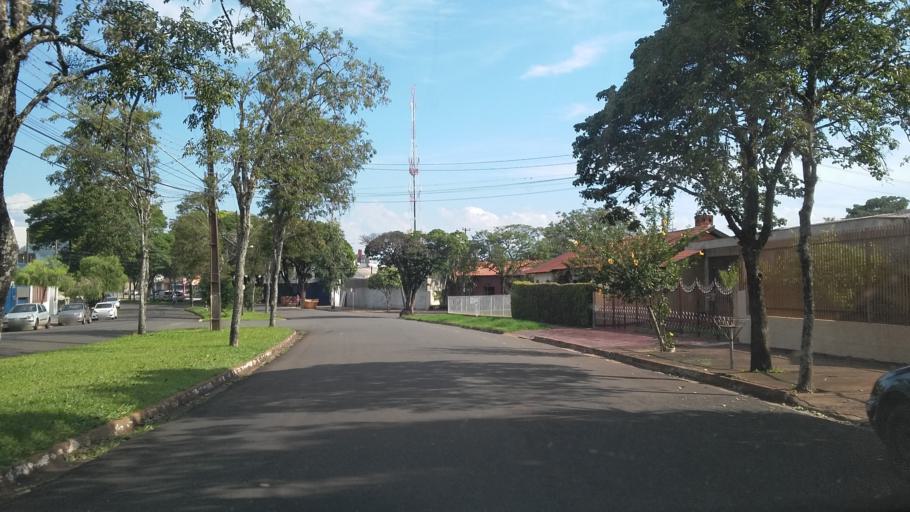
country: BR
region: Parana
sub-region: Londrina
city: Londrina
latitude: -23.2993
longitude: -51.1820
